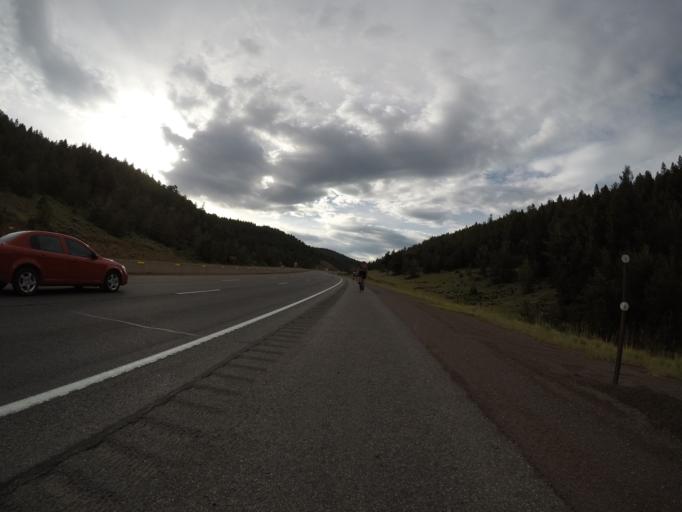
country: US
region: Wyoming
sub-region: Albany County
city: Laramie
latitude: 41.2626
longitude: -105.4631
